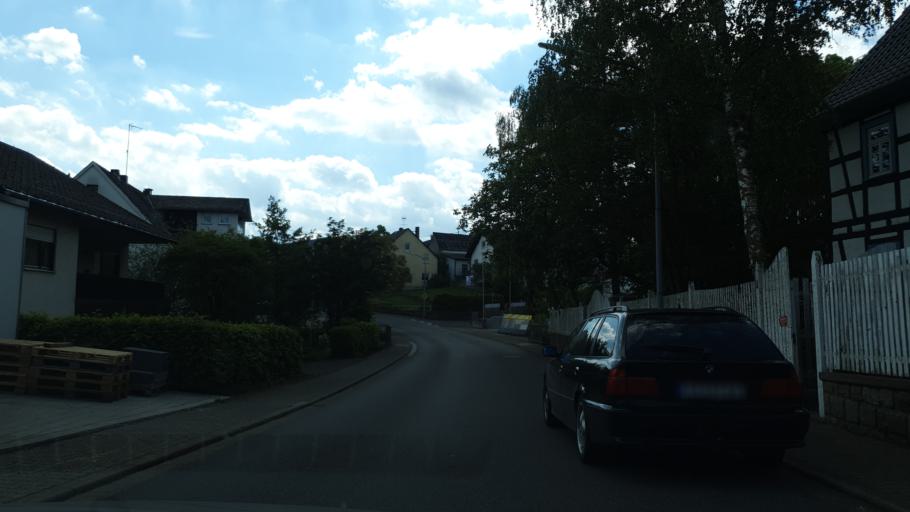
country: DE
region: Rheinland-Pfalz
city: Weidenhahn
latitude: 50.5442
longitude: 7.8329
